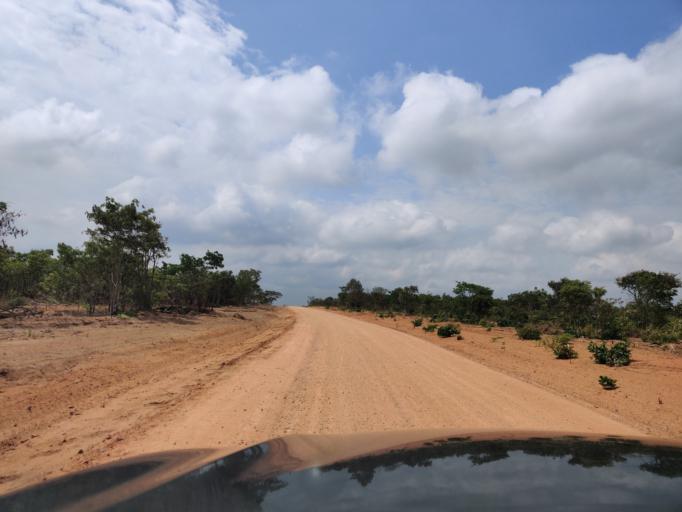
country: ZM
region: Central
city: Mkushi
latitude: -13.6646
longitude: 29.7510
